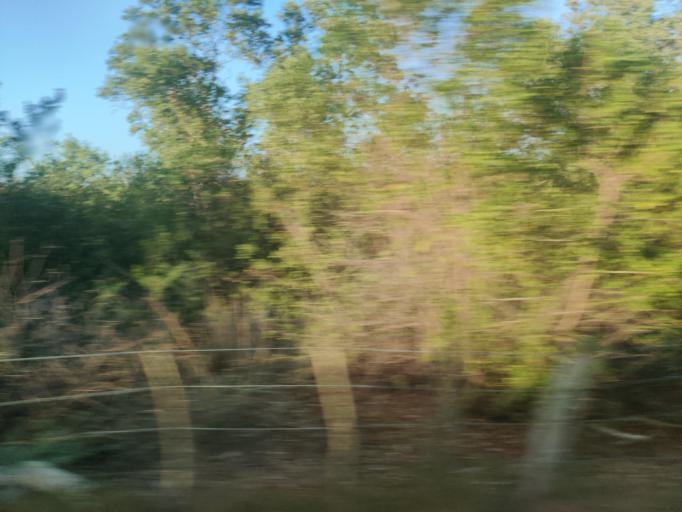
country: CO
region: Atlantico
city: Piojo
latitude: 10.7486
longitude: -75.2488
